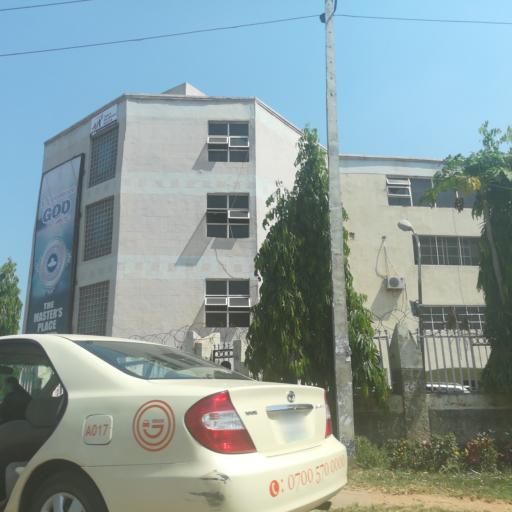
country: NG
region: Abuja Federal Capital Territory
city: Abuja
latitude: 9.0748
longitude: 7.4345
